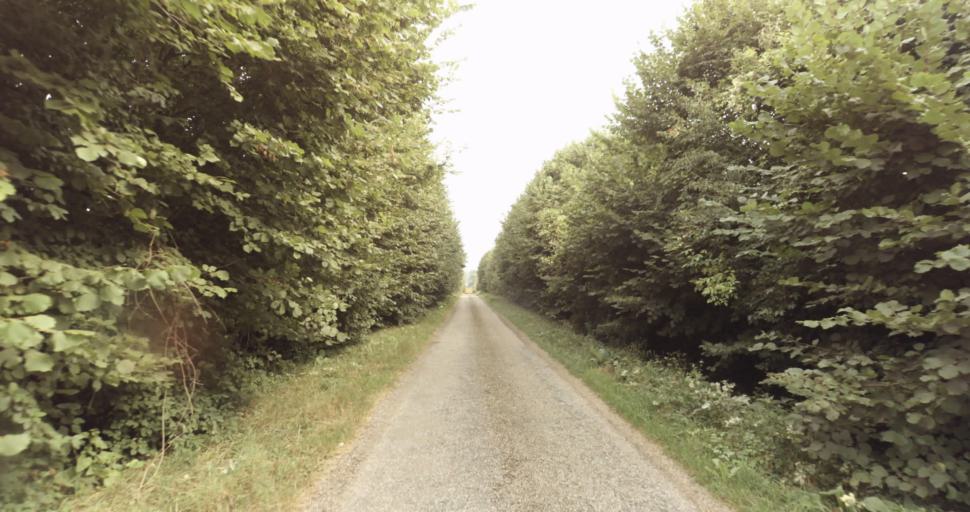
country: FR
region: Lower Normandy
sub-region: Departement de l'Orne
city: Vimoutiers
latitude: 48.9331
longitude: 0.2740
